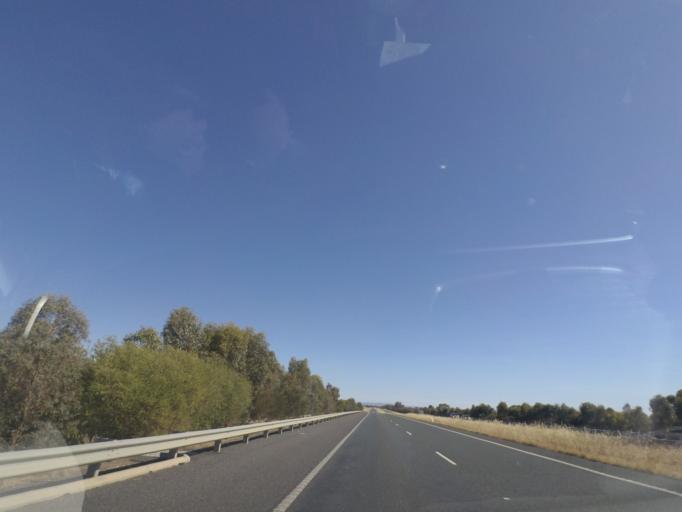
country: AU
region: Victoria
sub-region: Greater Shepparton
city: Shepparton
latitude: -36.7742
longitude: 145.1785
